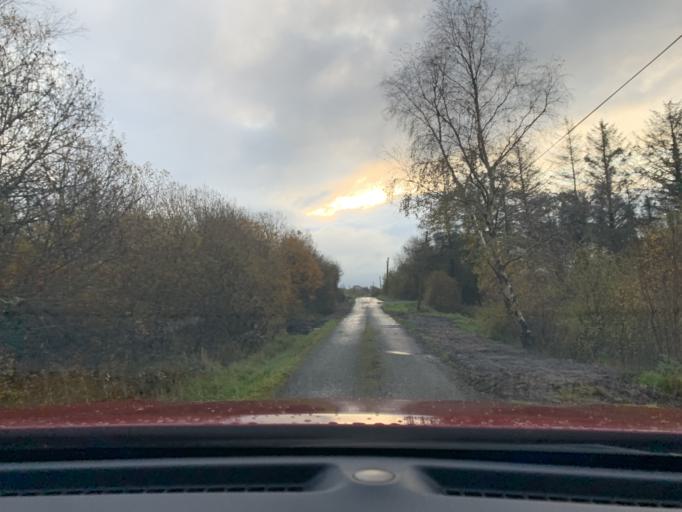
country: IE
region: Connaught
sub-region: Sligo
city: Ballymote
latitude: 54.0317
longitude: -8.5303
